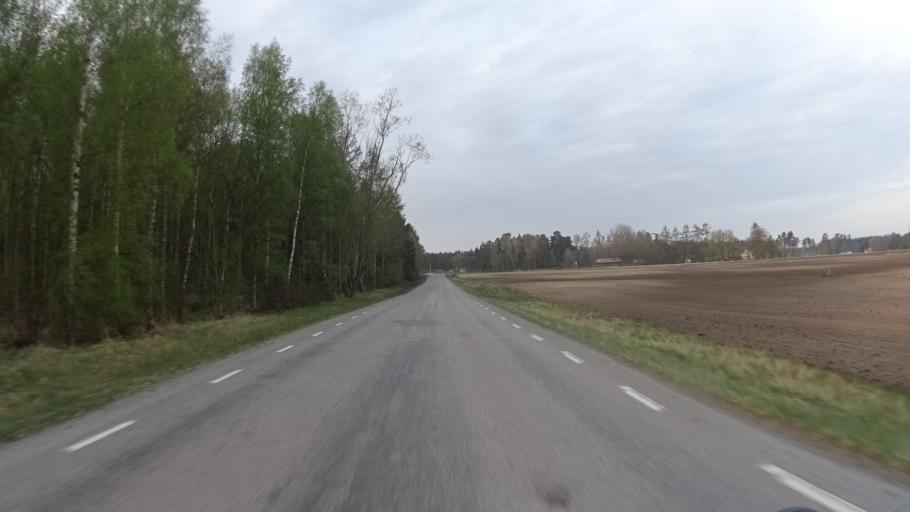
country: SE
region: Vaestra Goetaland
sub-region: Lidkopings Kommun
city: Vinninga
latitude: 58.4229
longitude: 13.3495
